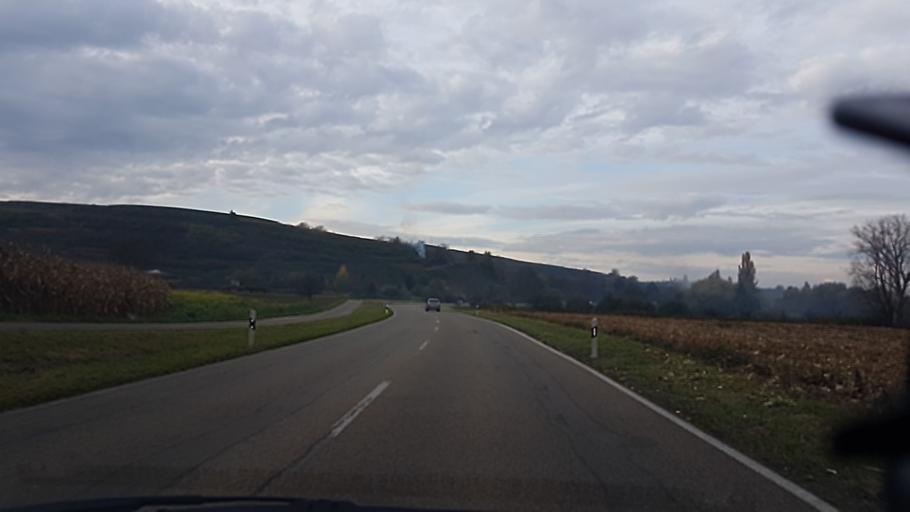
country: DE
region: Baden-Wuerttemberg
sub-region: Freiburg Region
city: Bahlingen
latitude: 48.1132
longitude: 7.7443
